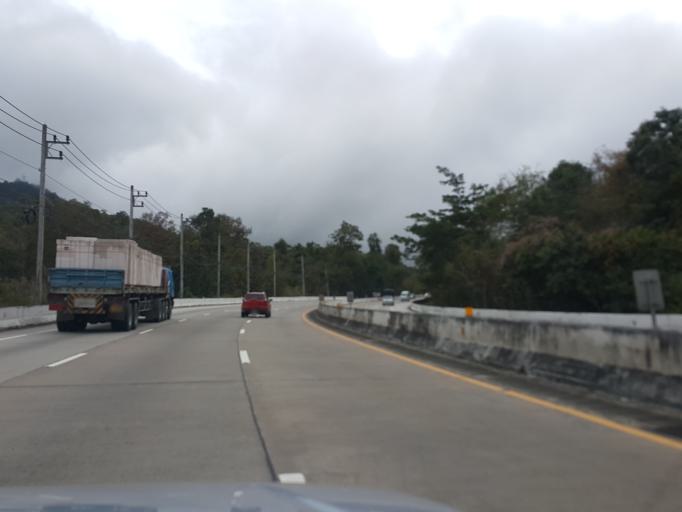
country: TH
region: Lamphun
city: Mae Tha
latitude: 18.4457
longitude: 99.2047
